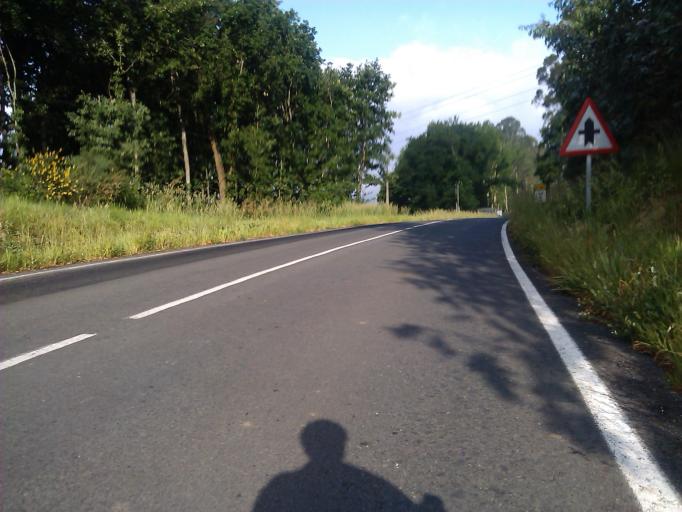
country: ES
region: Galicia
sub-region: Provincia da Coruna
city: Melide
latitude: 42.9055
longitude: -8.0438
